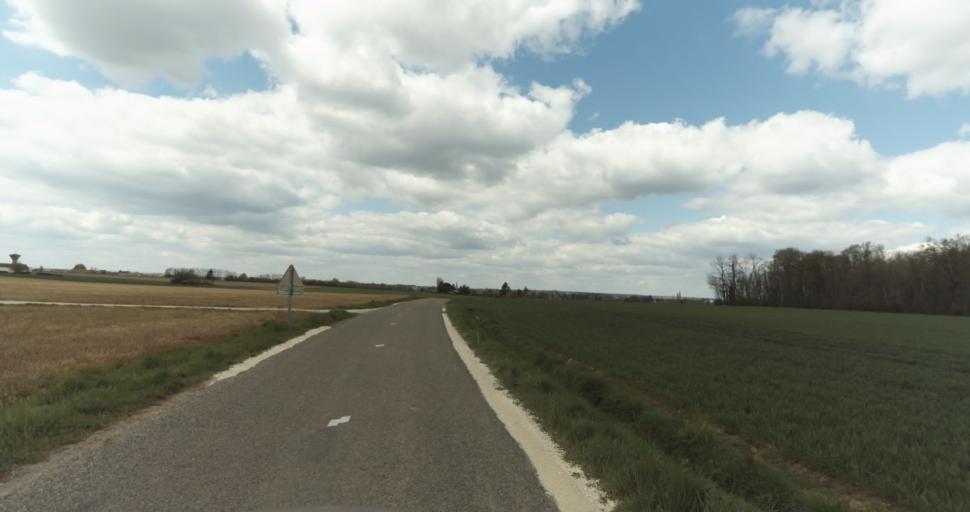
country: FR
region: Bourgogne
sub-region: Departement de la Cote-d'Or
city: Auxonne
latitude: 47.1823
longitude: 5.4134
